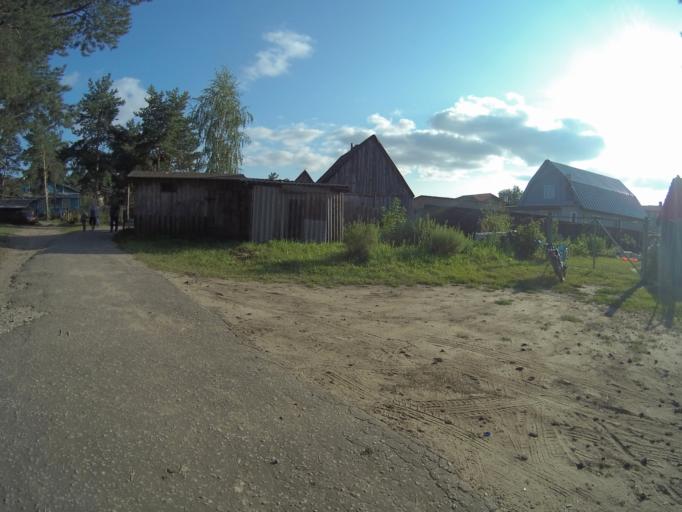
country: RU
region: Vladimir
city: Kommunar
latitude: 56.1227
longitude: 40.4610
